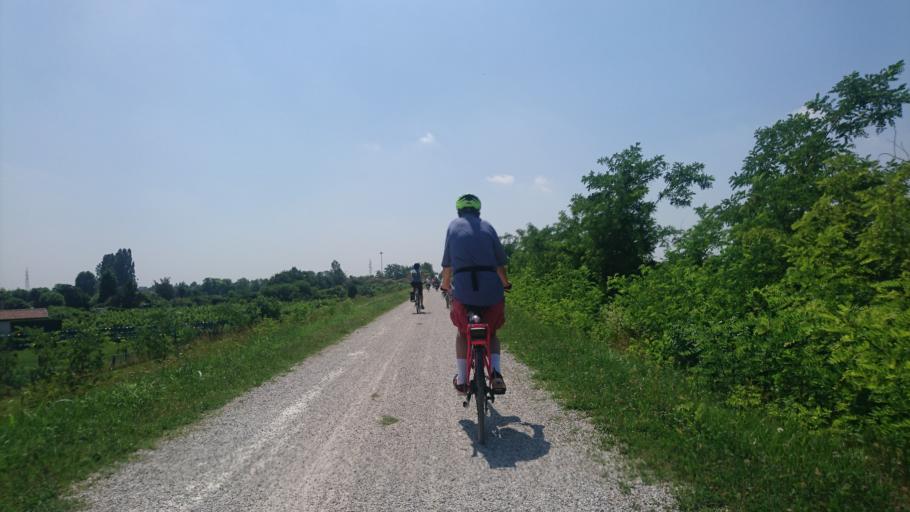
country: IT
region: Veneto
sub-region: Provincia di Venezia
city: Galta
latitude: 45.3888
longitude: 12.0151
